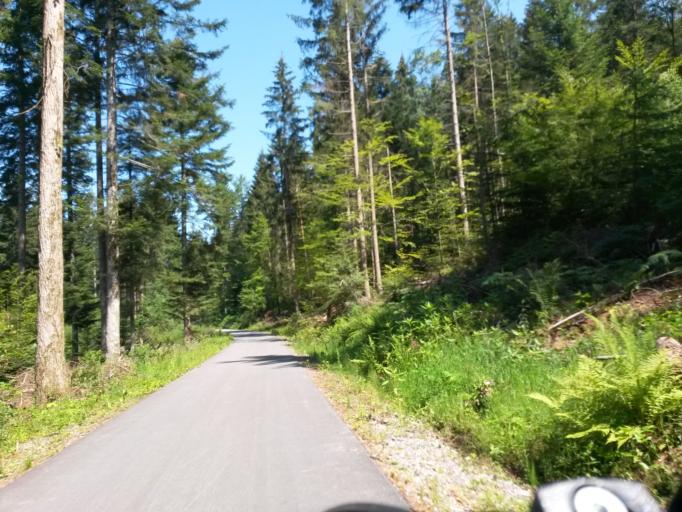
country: DE
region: Baden-Wuerttemberg
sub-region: Karlsruhe Region
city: Bad Wildbad
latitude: 48.7128
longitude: 8.5443
